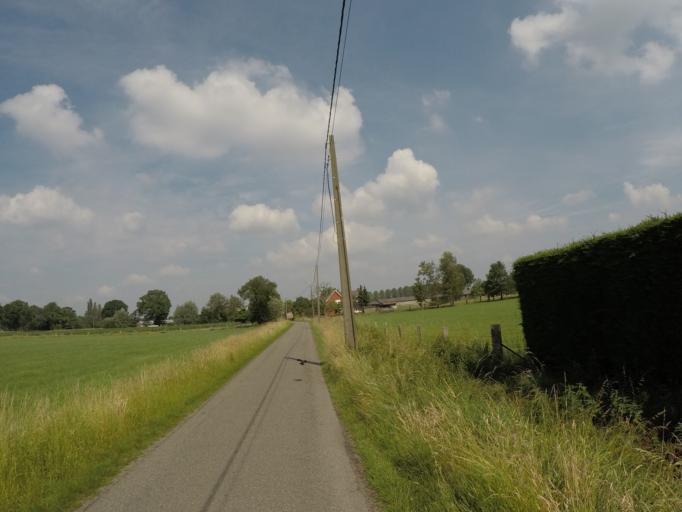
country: BE
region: Flanders
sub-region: Provincie Antwerpen
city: Brecht
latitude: 51.3359
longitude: 4.5912
